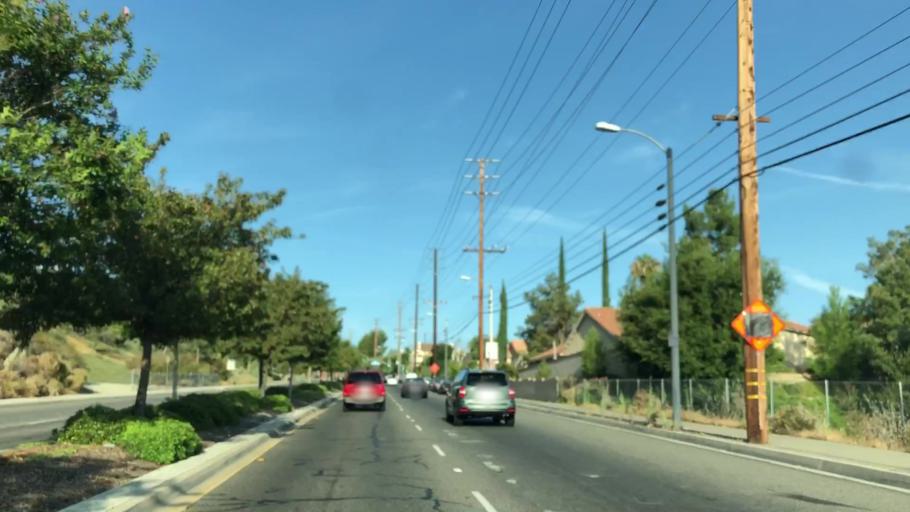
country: US
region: California
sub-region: Los Angeles County
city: Santa Clarita
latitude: 34.3983
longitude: -118.4780
